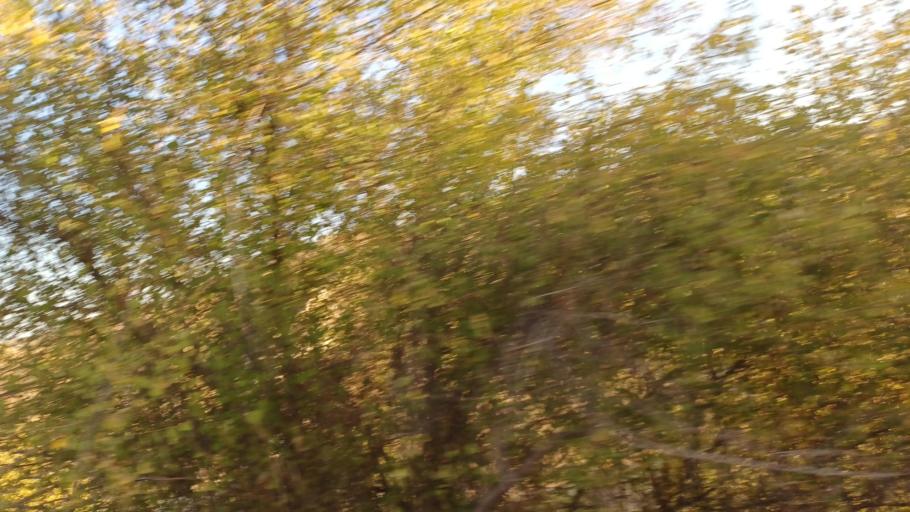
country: CY
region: Pafos
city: Tala
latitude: 34.9058
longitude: 32.5171
